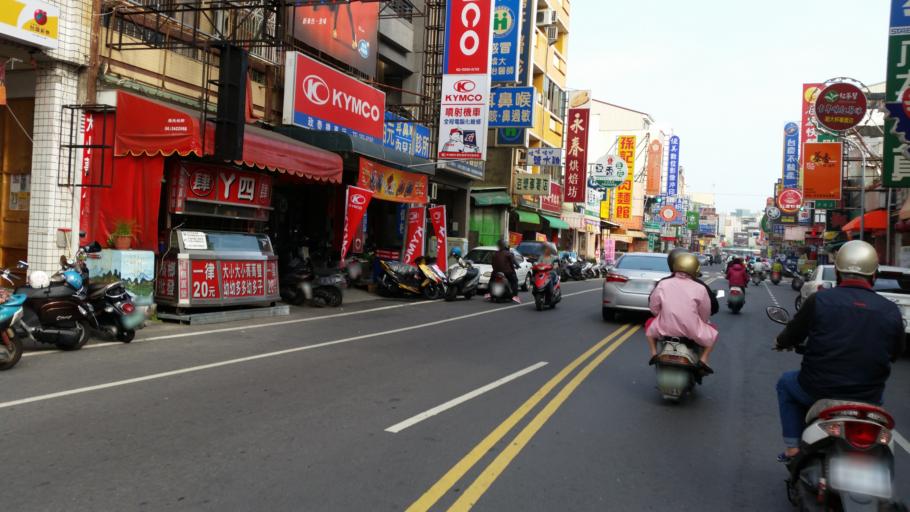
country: TW
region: Taiwan
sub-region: Tainan
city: Tainan
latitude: 22.9756
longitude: 120.2252
